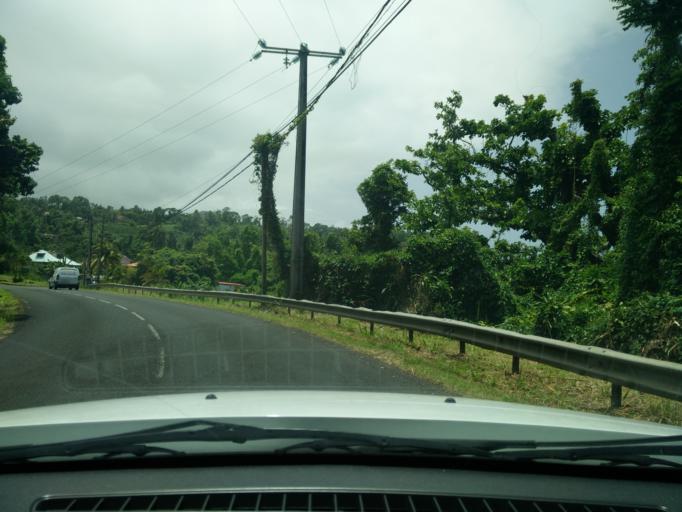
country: GP
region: Guadeloupe
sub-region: Guadeloupe
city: Trois-Rivieres
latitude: 15.9759
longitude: -61.6294
